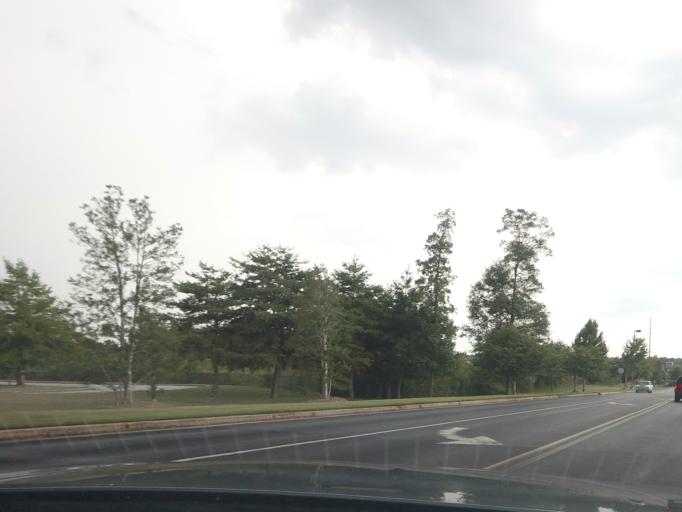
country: US
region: Georgia
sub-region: Bibb County
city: West Point
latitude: 32.8823
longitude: -83.7656
